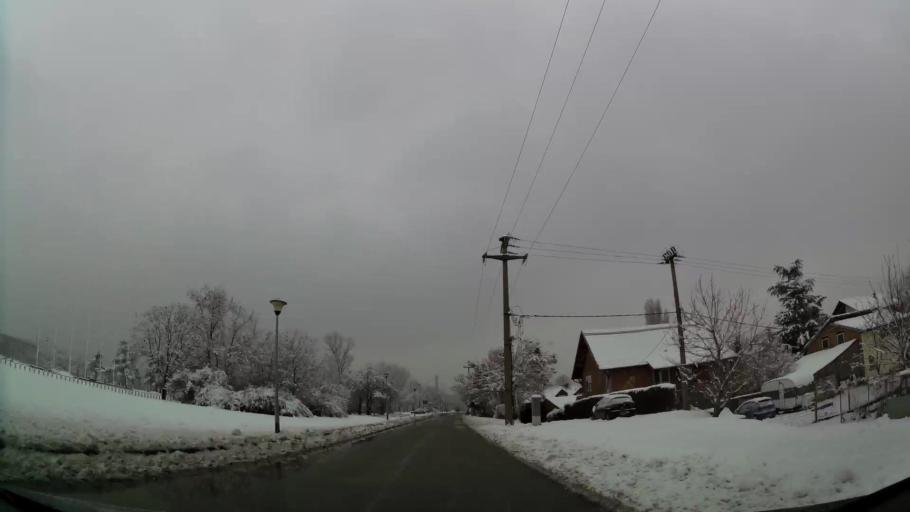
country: RS
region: Central Serbia
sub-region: Belgrade
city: Novi Beograd
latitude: 44.8069
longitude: 20.4414
